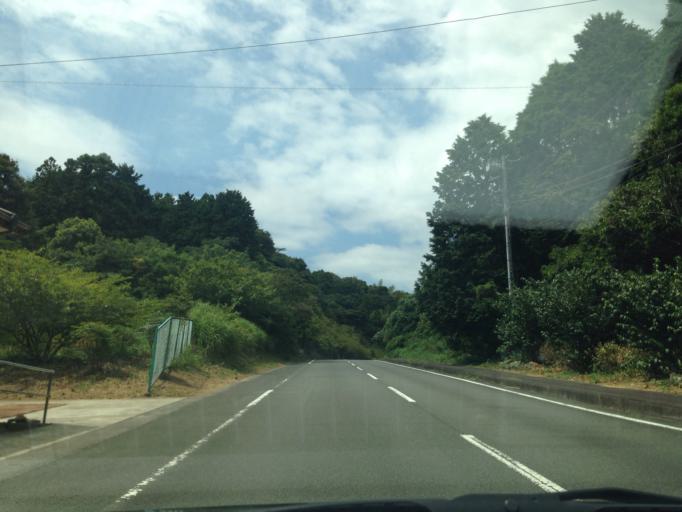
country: JP
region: Shizuoka
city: Shimoda
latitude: 34.6475
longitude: 138.8185
